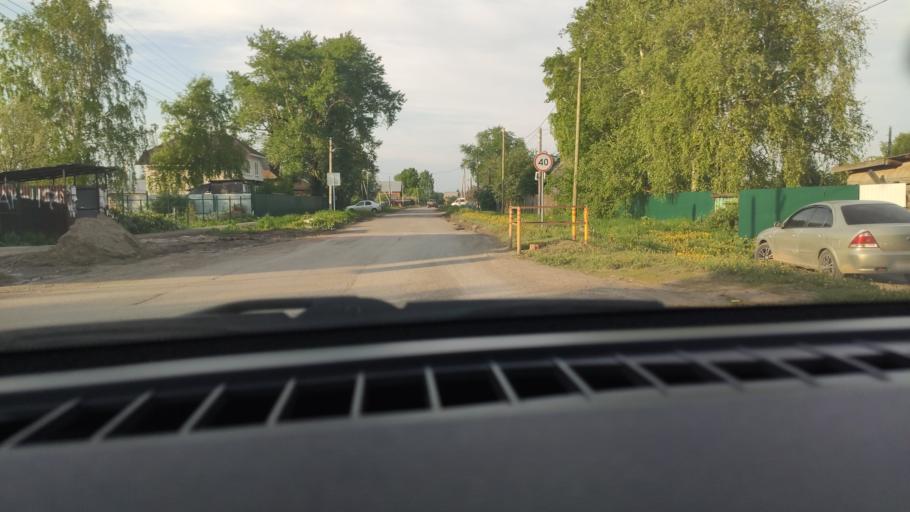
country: RU
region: Perm
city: Kultayevo
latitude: 57.9321
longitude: 56.0178
